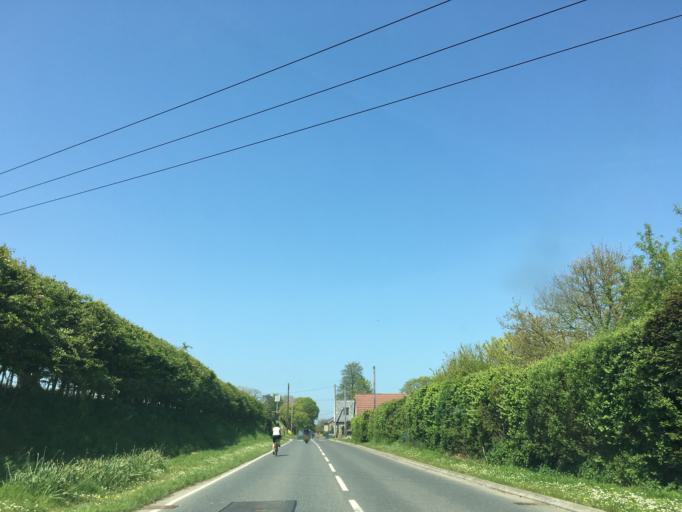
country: GB
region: England
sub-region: Isle of Wight
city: Niton
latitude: 50.5943
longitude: -1.2621
